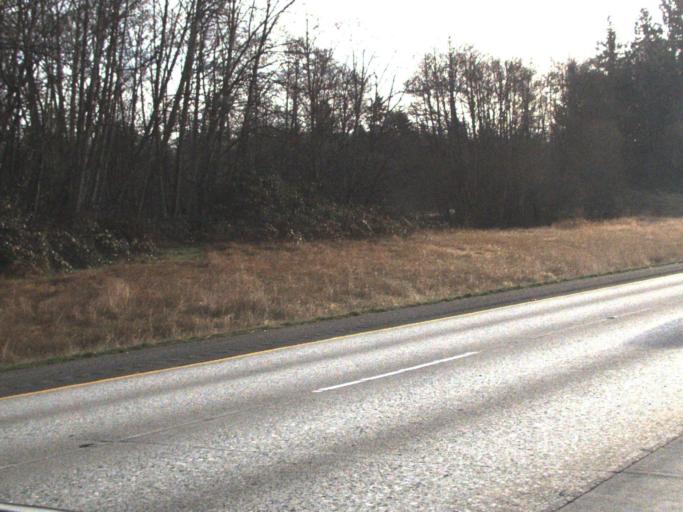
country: US
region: Washington
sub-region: Snohomish County
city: Bryant
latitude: 48.2534
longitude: -122.2562
